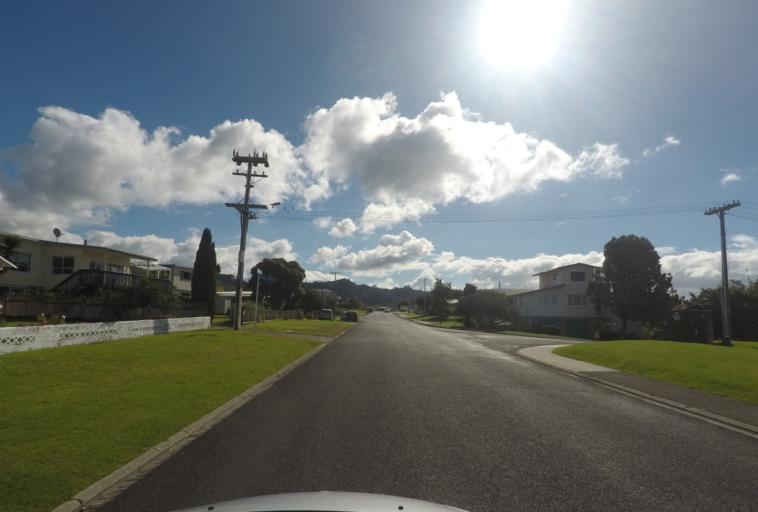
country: NZ
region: Bay of Plenty
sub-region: Western Bay of Plenty District
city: Waihi Beach
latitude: -37.4139
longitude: 175.9430
